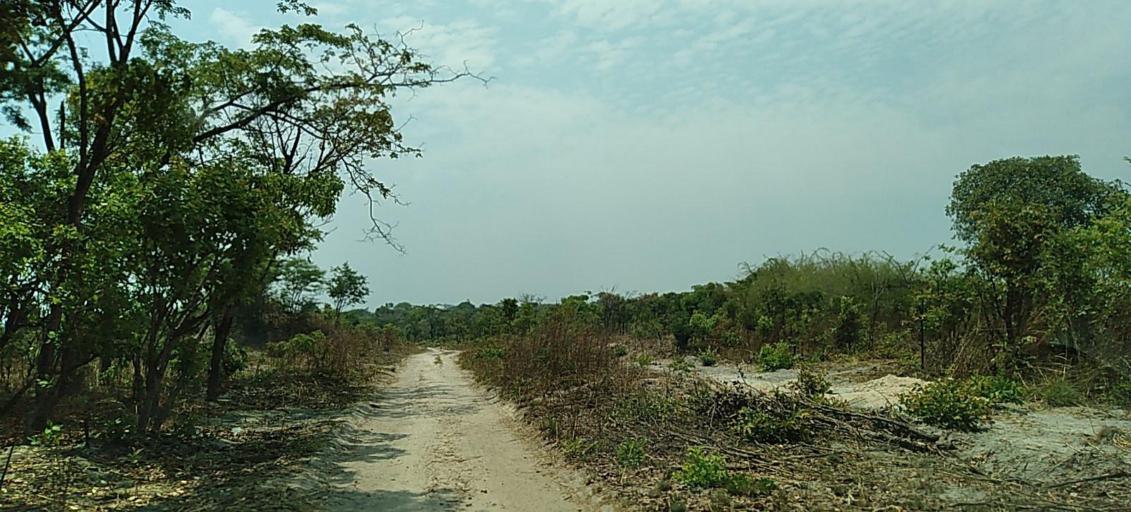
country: ZM
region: Copperbelt
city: Kalulushi
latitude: -12.9401
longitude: 28.1172
